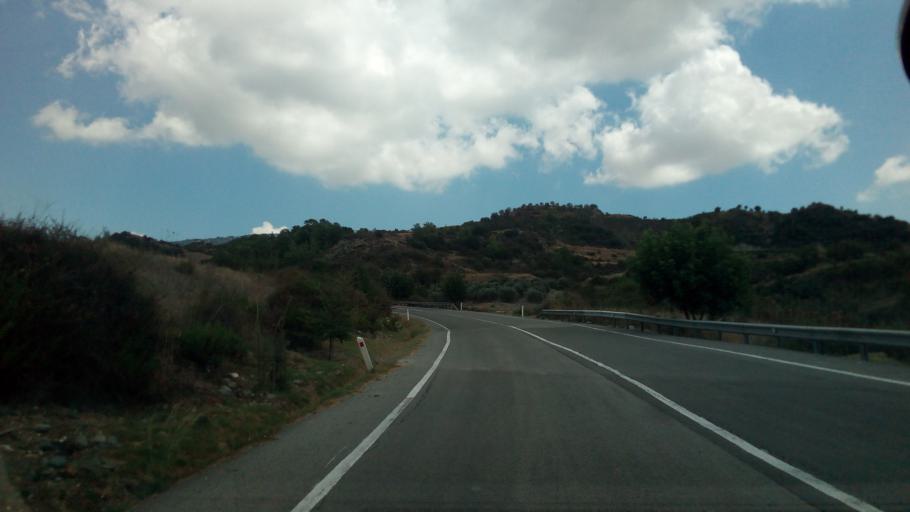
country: CY
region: Pafos
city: Mesogi
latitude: 34.9228
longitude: 32.5856
